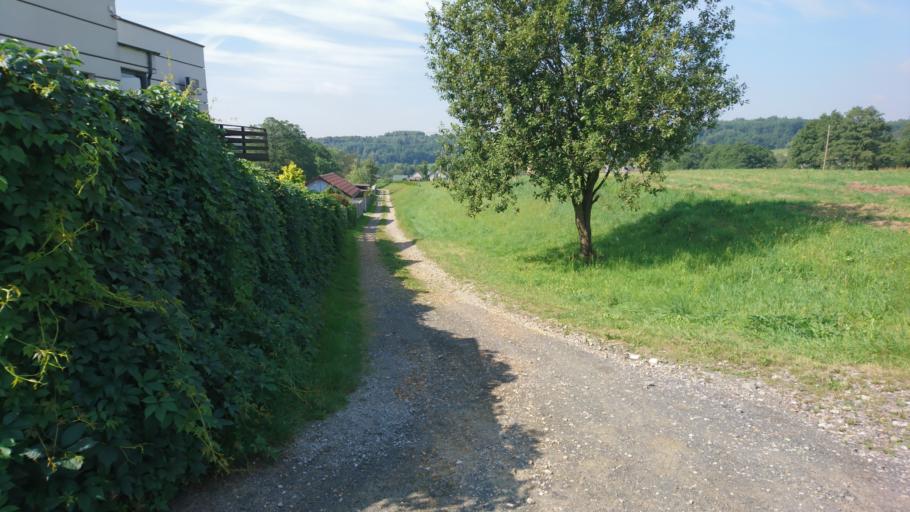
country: PL
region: Lesser Poland Voivodeship
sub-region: Powiat krakowski
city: Filipowice
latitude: 50.1555
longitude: 19.5712
